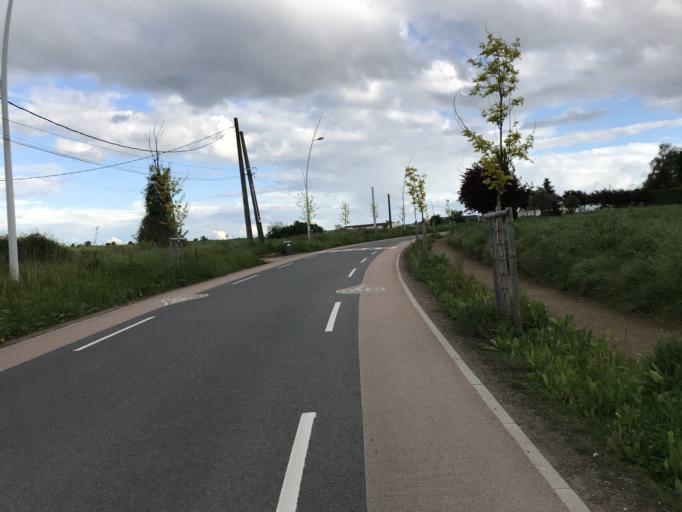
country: FR
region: Ile-de-France
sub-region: Departement de l'Essonne
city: Wissous
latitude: 48.7386
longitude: 2.3368
